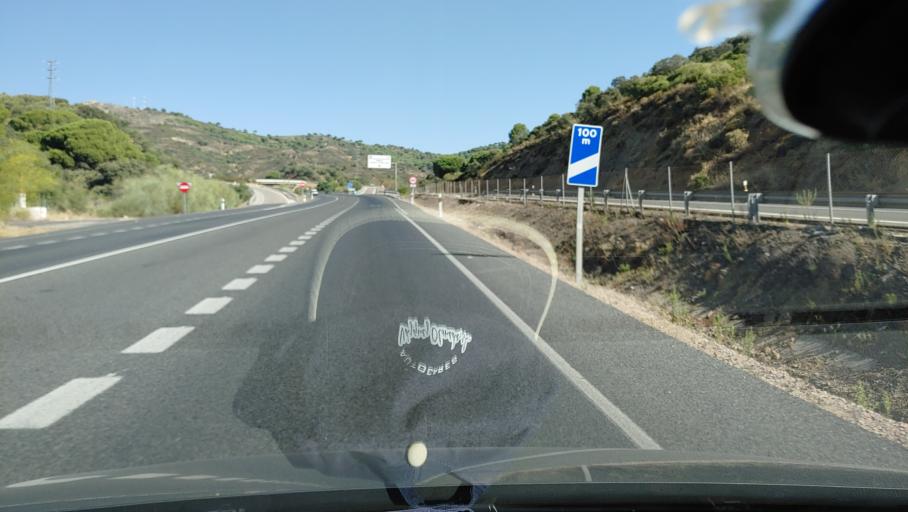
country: ES
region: Andalusia
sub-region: Province of Cordoba
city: Cordoba
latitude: 37.9704
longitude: -4.7691
